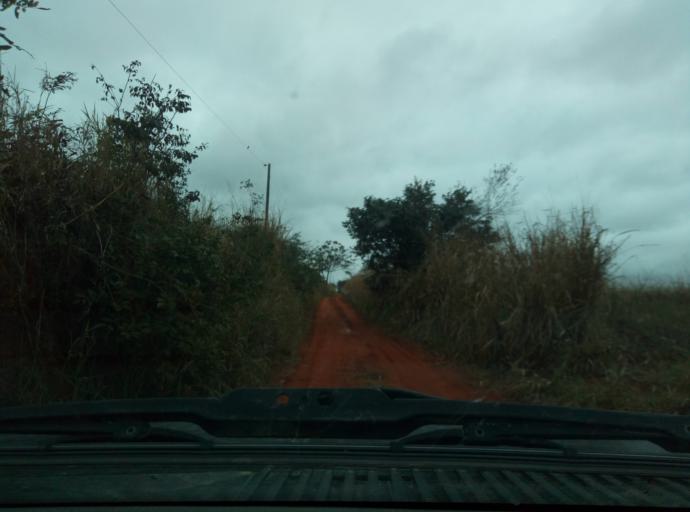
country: PY
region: Caaguazu
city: Doctor Cecilio Baez
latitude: -25.1592
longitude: -56.2717
